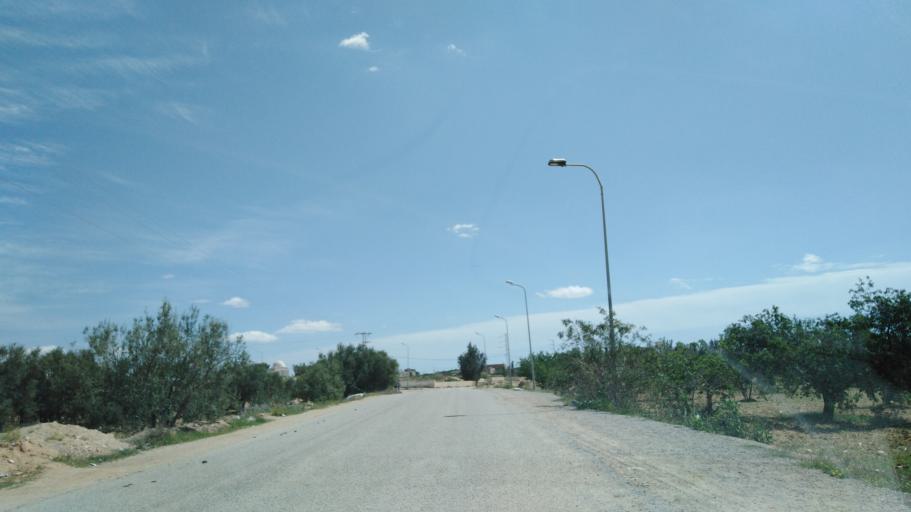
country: TN
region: Safaqis
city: Sfax
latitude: 34.7400
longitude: 10.5380
